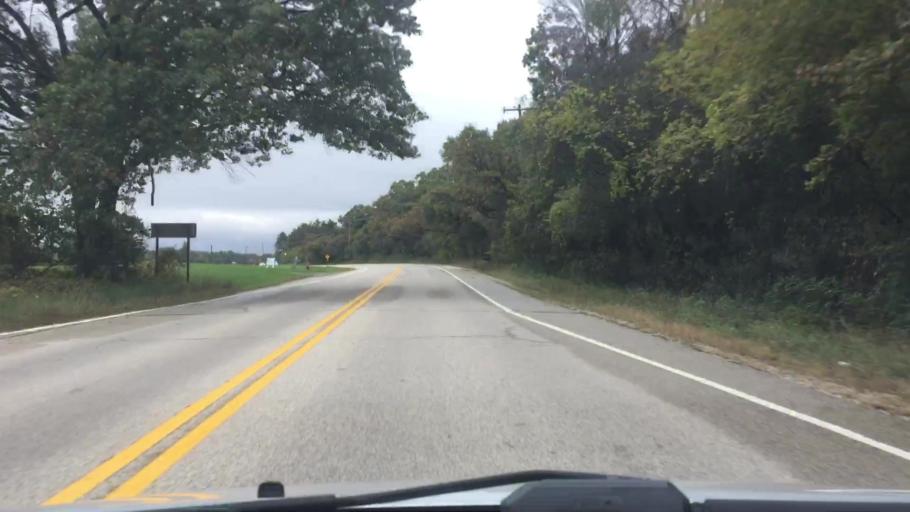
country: US
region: Wisconsin
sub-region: Waukesha County
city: Eagle
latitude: 42.8634
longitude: -88.4878
